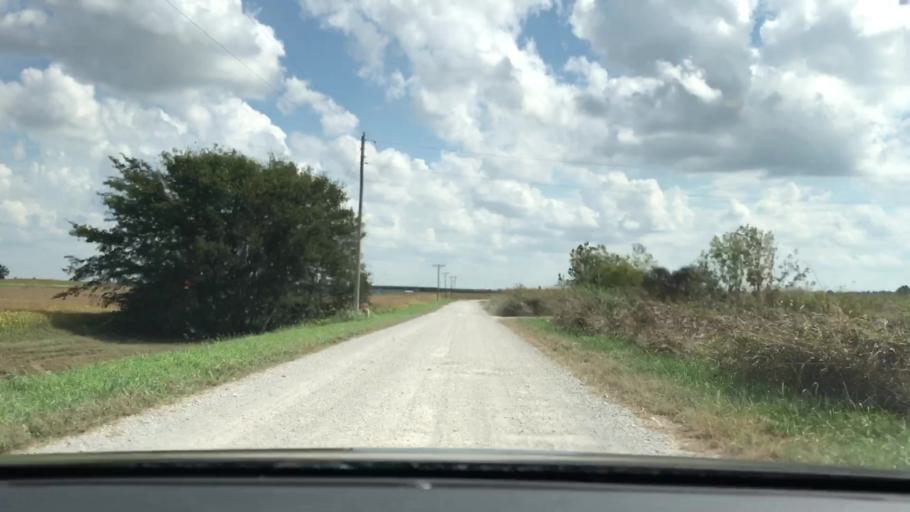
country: US
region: Kentucky
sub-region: Christian County
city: Oak Grove
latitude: 36.6828
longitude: -87.4102
